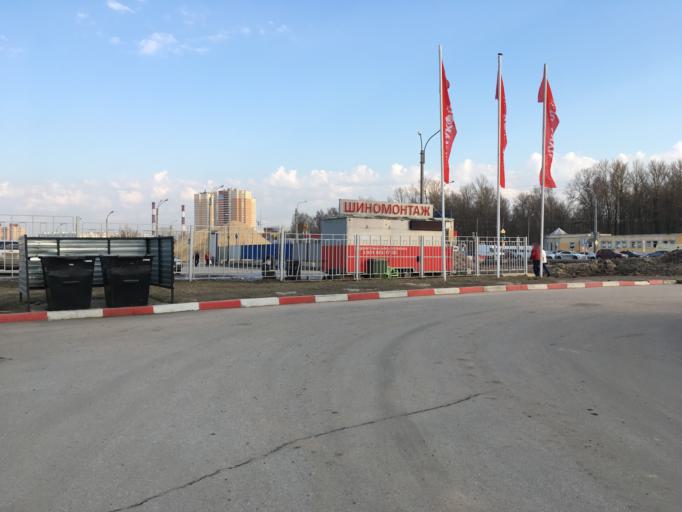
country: RU
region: St.-Petersburg
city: Komendantsky aerodrom
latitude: 60.0010
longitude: 30.2624
